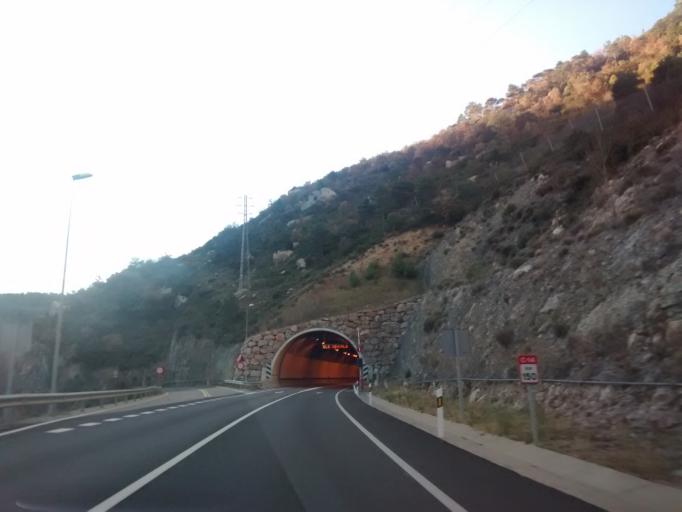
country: ES
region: Catalonia
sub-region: Provincia de Lleida
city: Coll de Nargo
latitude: 42.1333
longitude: 1.3097
